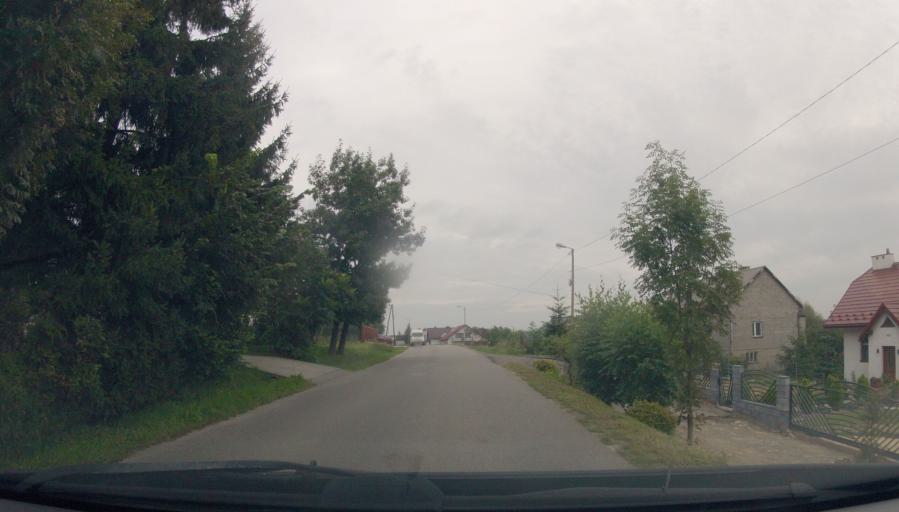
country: PL
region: Lesser Poland Voivodeship
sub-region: Powiat wielicki
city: Pawlikowice
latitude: 49.9505
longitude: 20.0177
